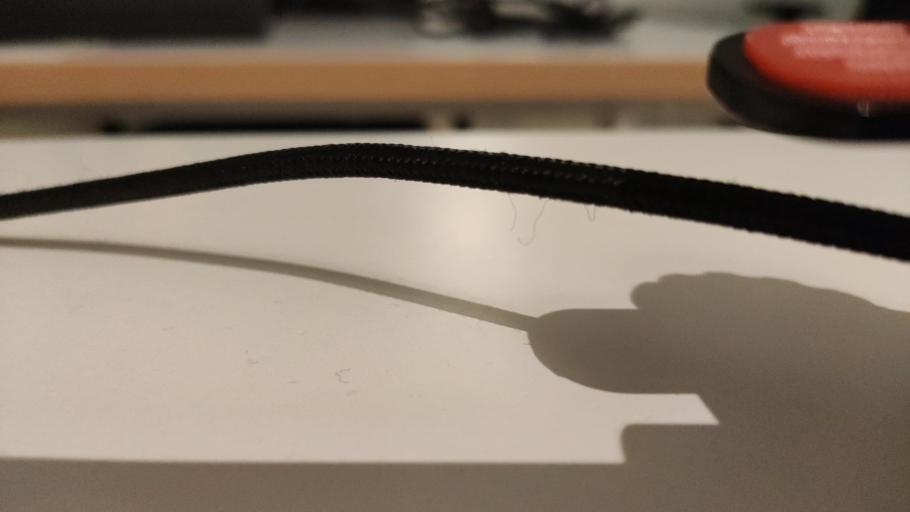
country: RU
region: Moskovskaya
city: Gorshkovo
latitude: 56.3726
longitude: 37.3797
